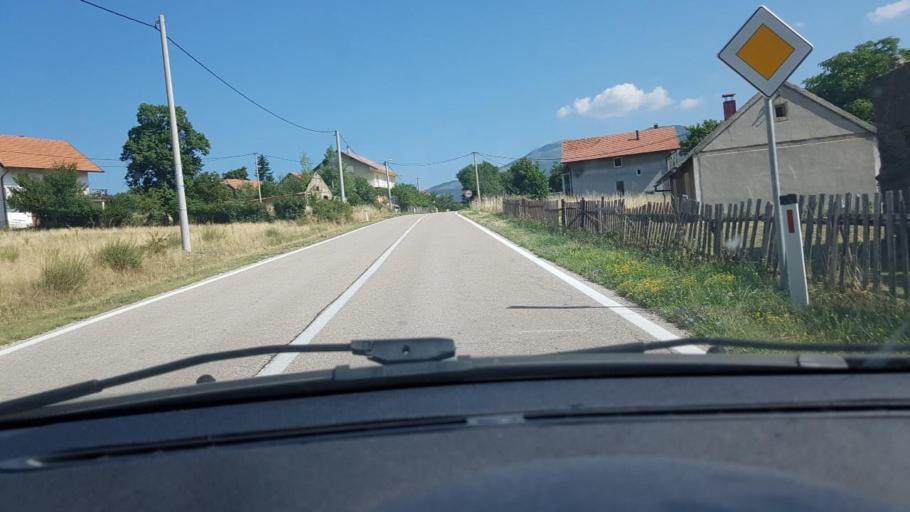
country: BA
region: Federation of Bosnia and Herzegovina
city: Bosansko Grahovo
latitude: 44.0770
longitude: 16.5712
